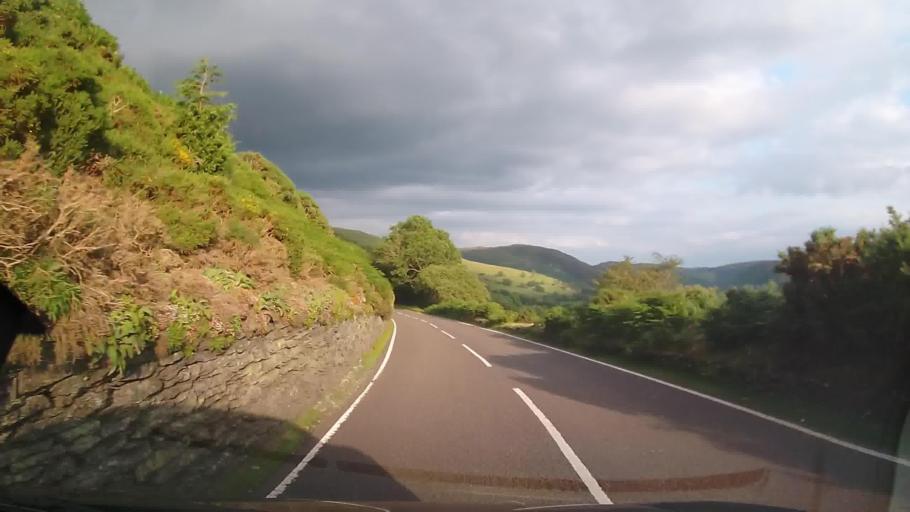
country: GB
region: Wales
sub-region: Sir Powys
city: Llangynog
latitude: 52.8517
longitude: -3.4382
